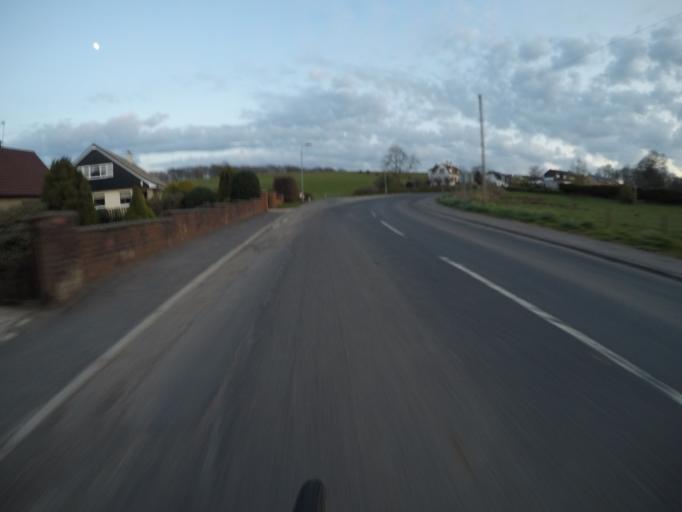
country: GB
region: Scotland
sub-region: South Ayrshire
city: Dundonald
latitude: 55.5733
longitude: -4.5916
